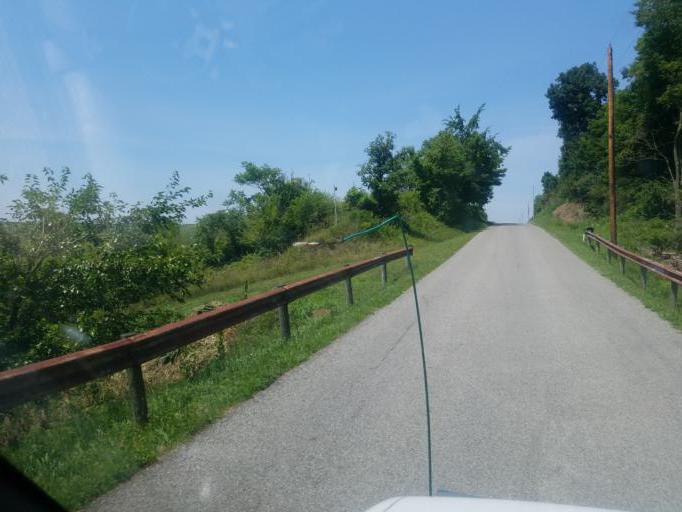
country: US
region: Ohio
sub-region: Logan County
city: De Graff
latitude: 40.2931
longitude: -83.8348
